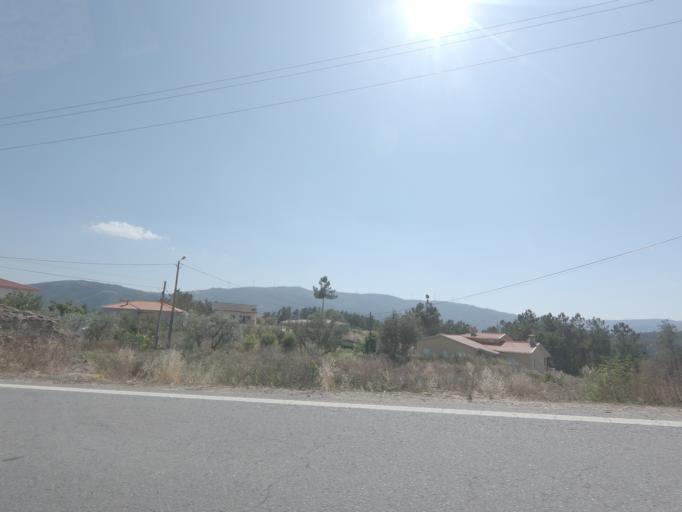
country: PT
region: Viseu
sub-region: Tarouca
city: Tarouca
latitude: 41.0310
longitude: -7.7475
